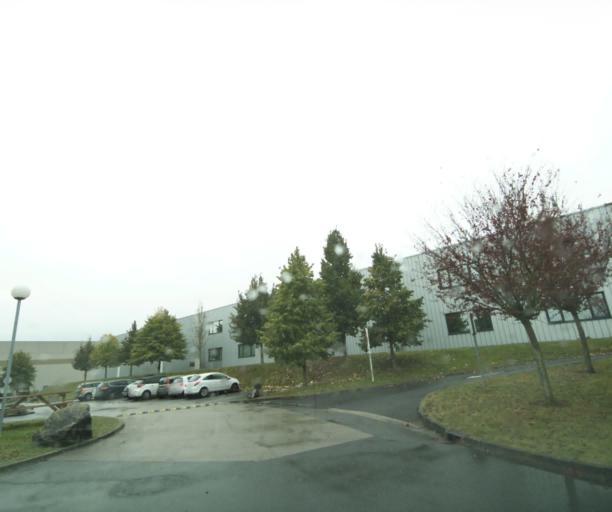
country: FR
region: Nord-Pas-de-Calais
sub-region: Departement du Nord
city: Roncq
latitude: 50.7551
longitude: 3.1322
